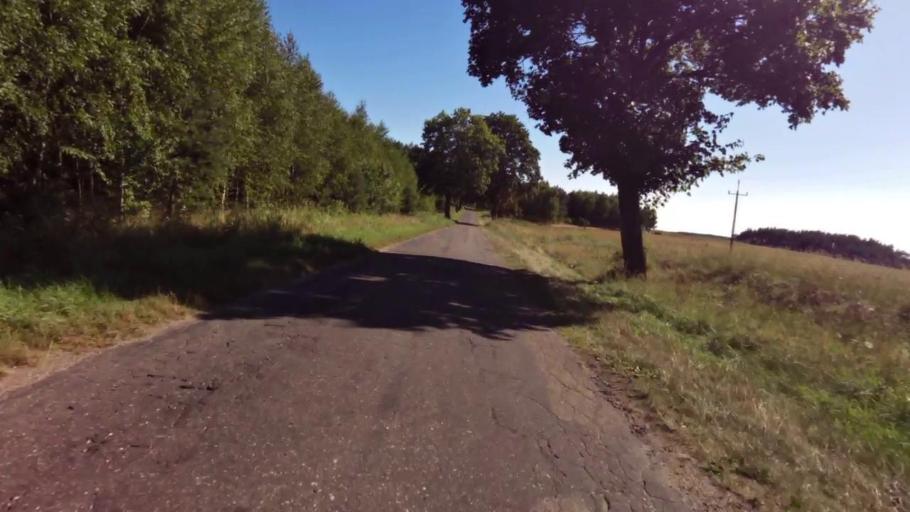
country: PL
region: West Pomeranian Voivodeship
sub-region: Powiat szczecinecki
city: Szczecinek
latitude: 53.7888
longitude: 16.6777
